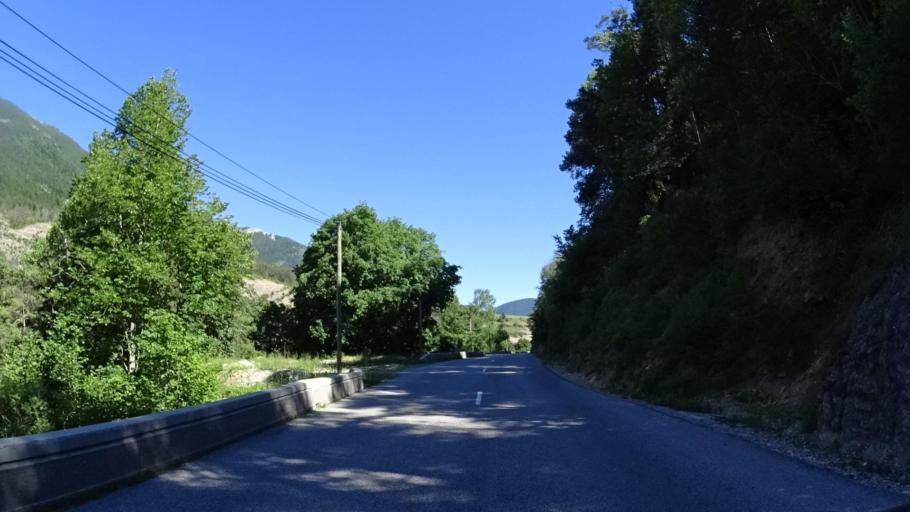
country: FR
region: Provence-Alpes-Cote d'Azur
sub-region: Departement des Alpes-de-Haute-Provence
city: Annot
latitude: 44.0165
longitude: 6.5582
